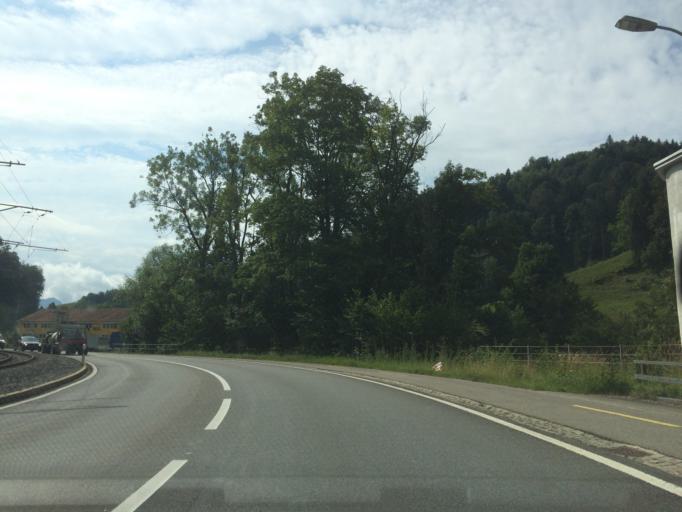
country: CH
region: Appenzell Ausserrhoden
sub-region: Bezirk Mittelland
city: Buhler
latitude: 47.3674
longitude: 9.4311
